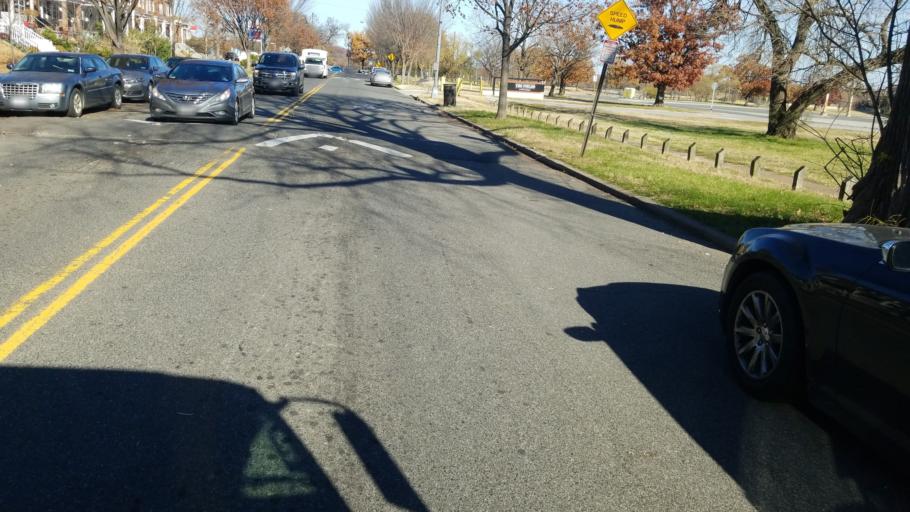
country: US
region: Maryland
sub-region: Prince George's County
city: Colmar Manor
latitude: 38.8963
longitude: -76.9706
